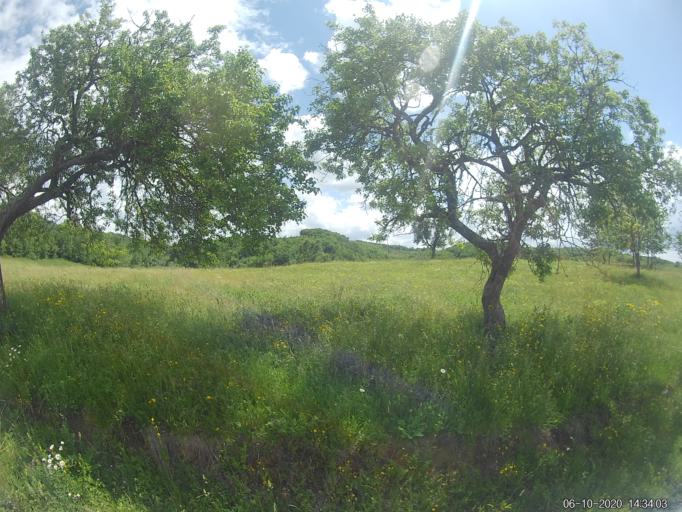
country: XK
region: Prizren
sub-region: Komuna e Therandes
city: Budakovo
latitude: 42.4160
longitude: 20.9288
